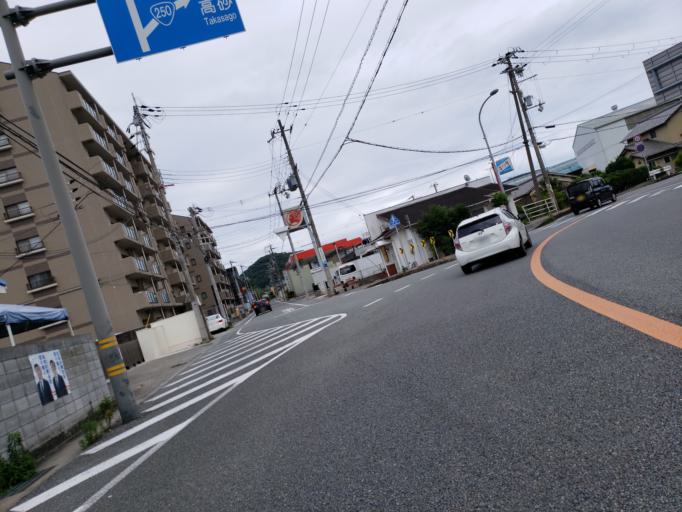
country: JP
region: Hyogo
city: Shirahamacho-usazakiminami
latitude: 34.7851
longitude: 134.7182
